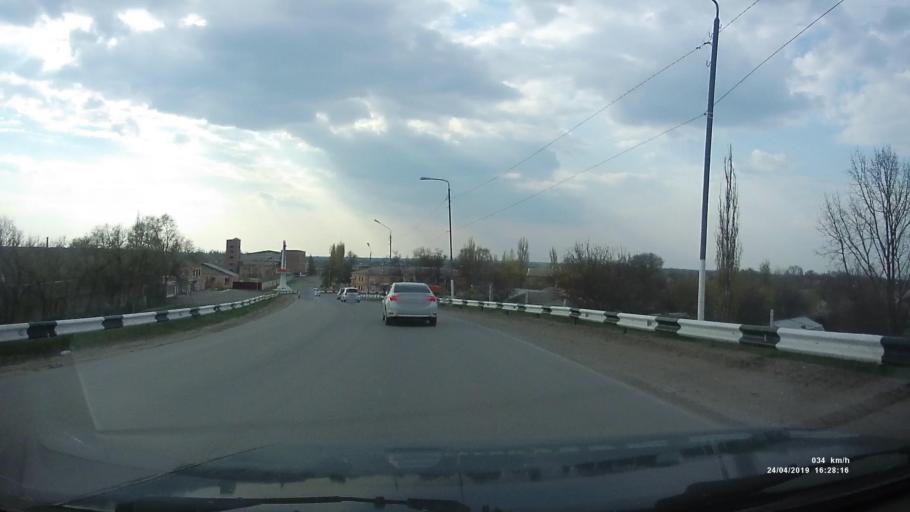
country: RU
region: Rostov
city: Orlovskiy
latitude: 46.8645
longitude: 42.0356
